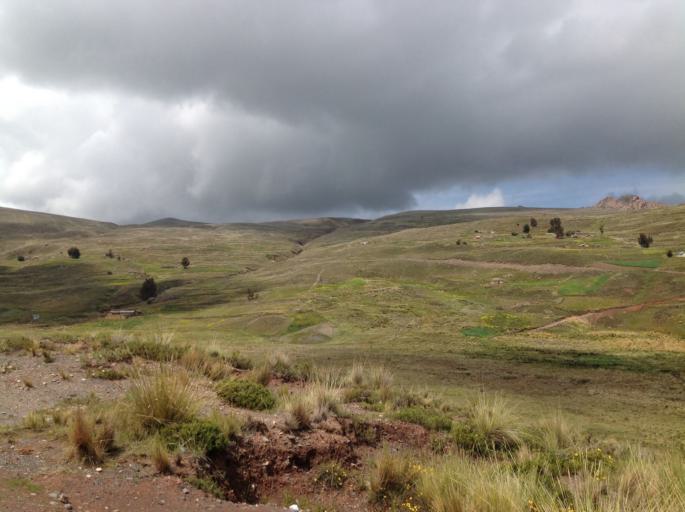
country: BO
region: La Paz
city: Yumani
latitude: -15.7684
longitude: -68.9860
